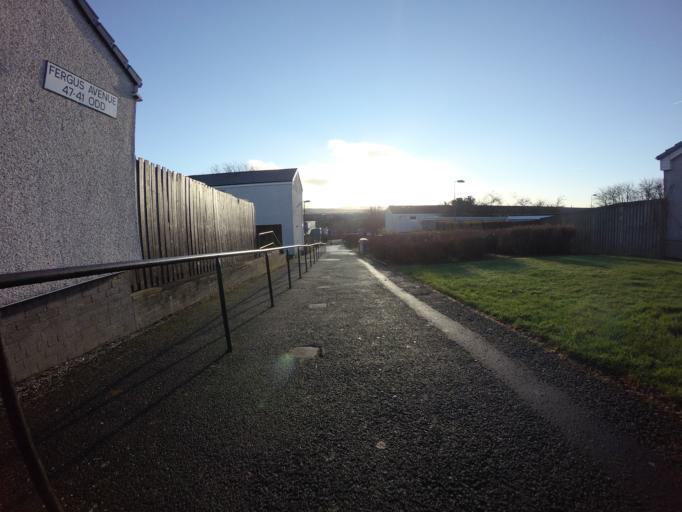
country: GB
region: Scotland
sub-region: West Lothian
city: Livingston
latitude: 55.8937
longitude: -3.5104
